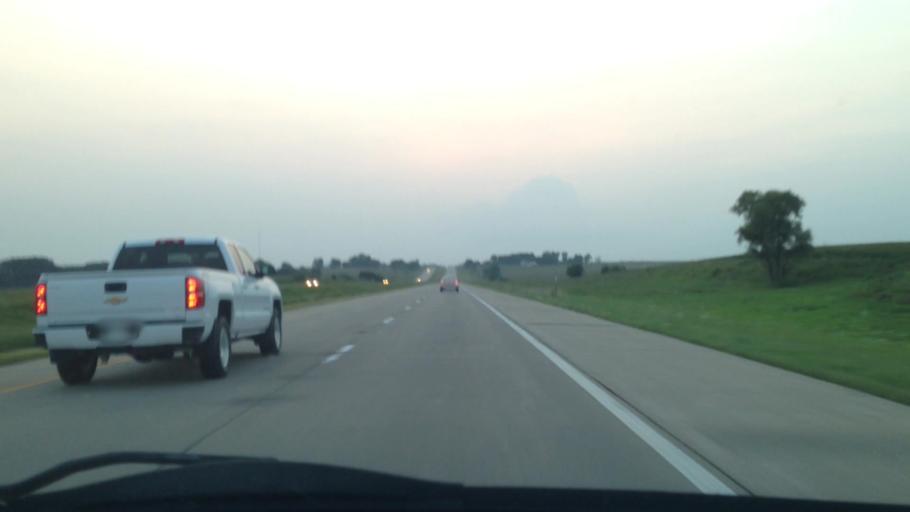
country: US
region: Iowa
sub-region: Buchanan County
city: Jesup
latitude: 42.3344
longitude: -92.0112
